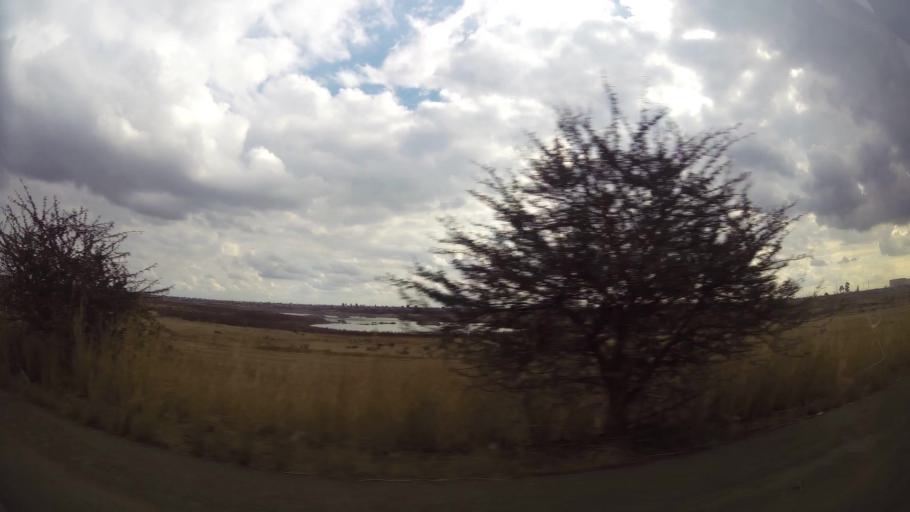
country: ZA
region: Orange Free State
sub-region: Fezile Dabi District Municipality
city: Sasolburg
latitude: -26.8676
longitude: 27.8876
